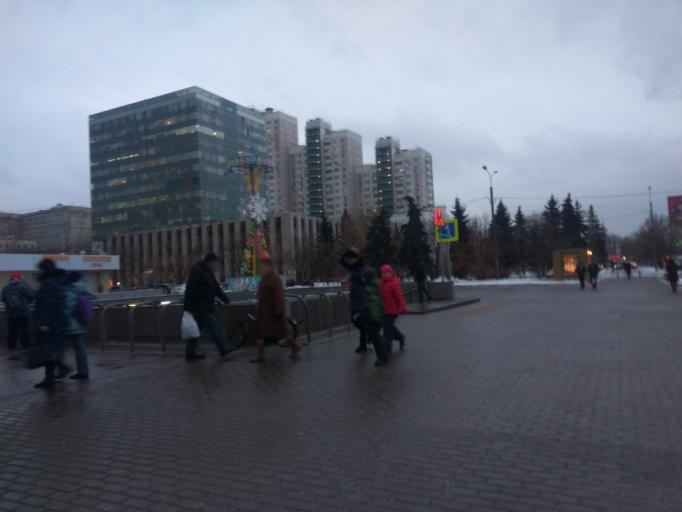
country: RU
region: Moscow
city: Perovo
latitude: 55.7514
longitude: 37.7885
